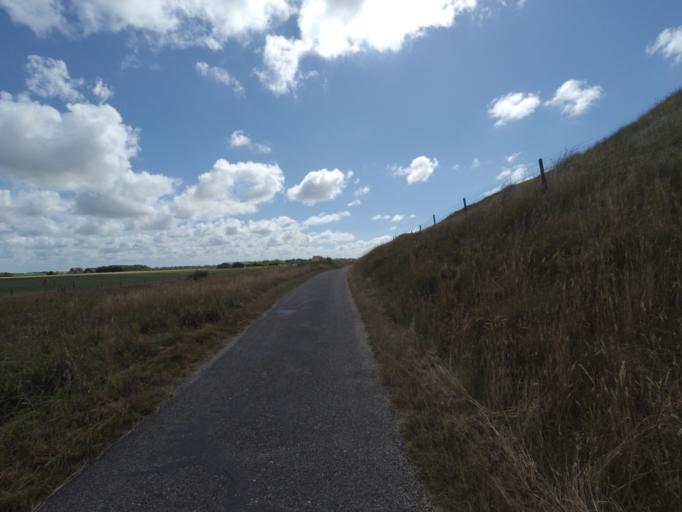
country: NL
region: North Holland
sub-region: Gemeente Texel
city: Den Burg
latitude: 53.1339
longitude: 4.8199
